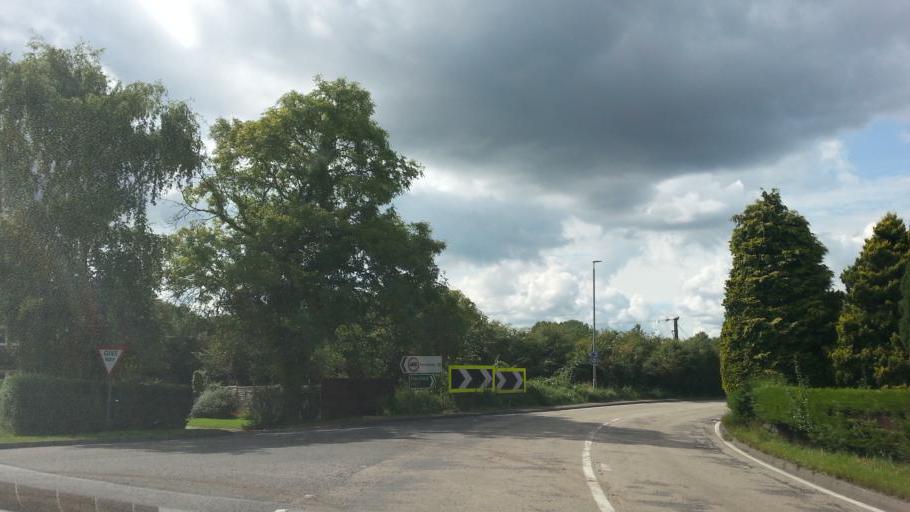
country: GB
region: England
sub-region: Nottinghamshire
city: Southwell
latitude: 53.1115
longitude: -0.9804
